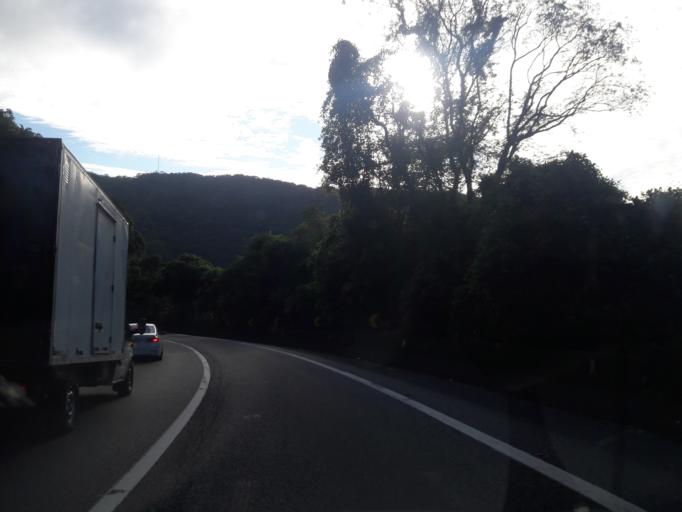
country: BR
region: Sao Paulo
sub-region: Cubatao
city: Cubatao
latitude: -23.8911
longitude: -46.4923
